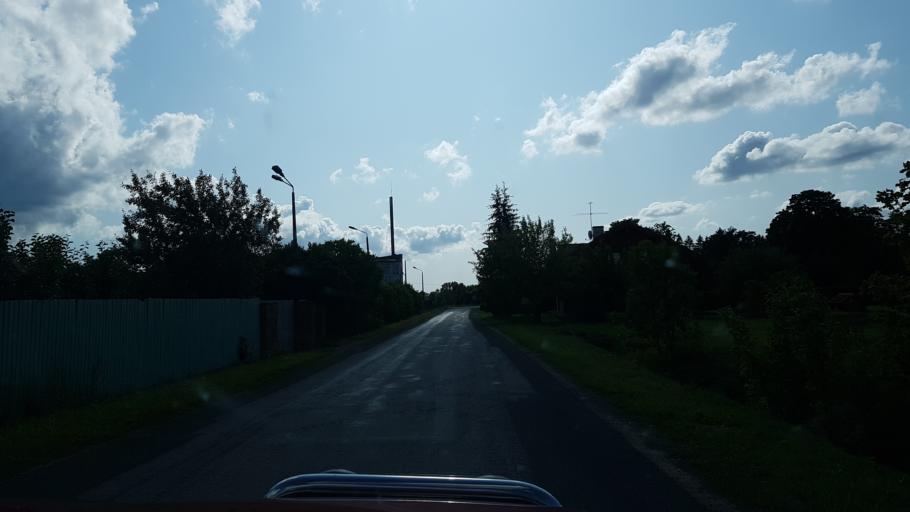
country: EE
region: Harju
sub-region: Paldiski linn
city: Paldiski
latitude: 59.2304
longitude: 24.0038
